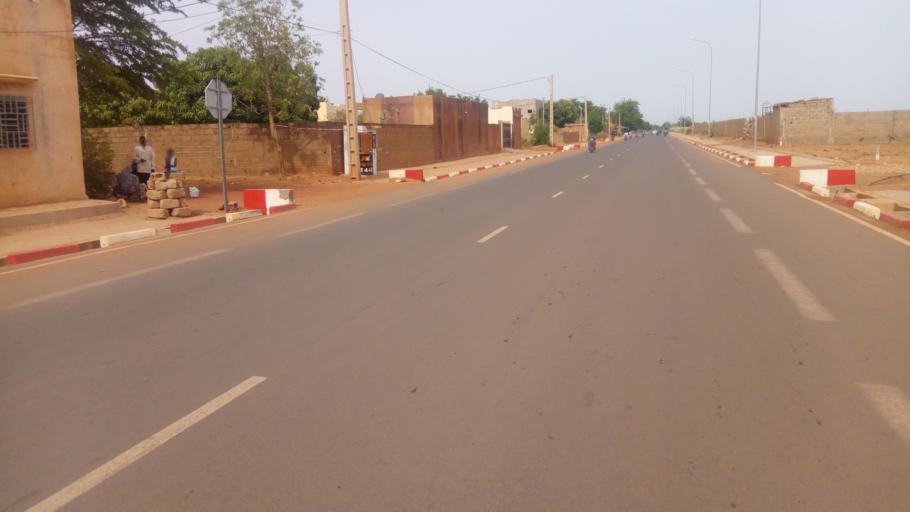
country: ML
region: Segou
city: Segou
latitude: 13.4322
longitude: -6.2746
